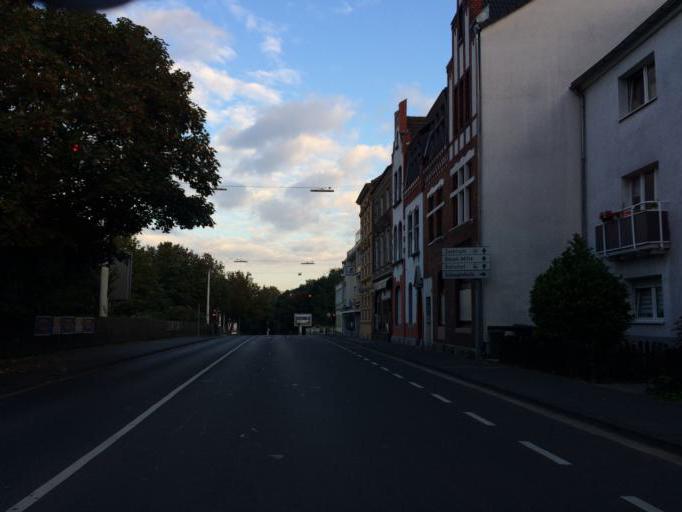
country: DE
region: North Rhine-Westphalia
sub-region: Regierungsbezirk Koln
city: Bonn
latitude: 50.7394
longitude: 7.1283
